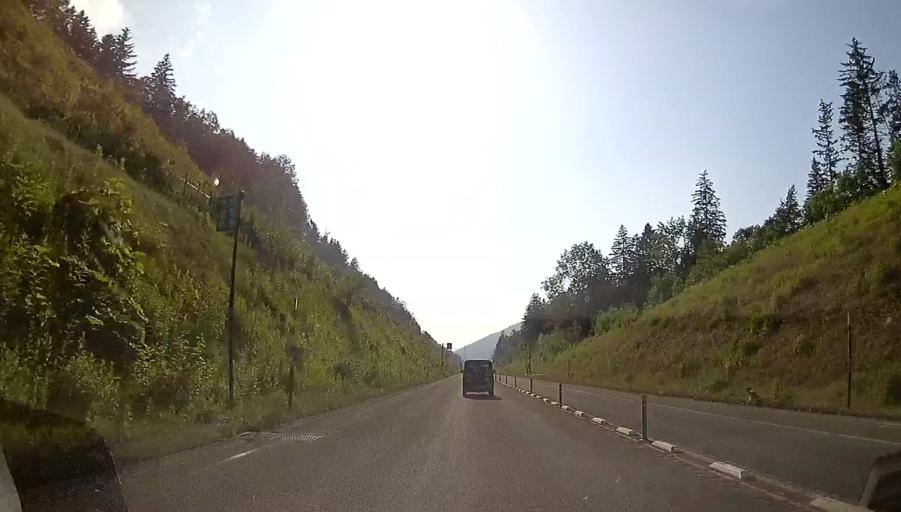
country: JP
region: Hokkaido
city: Shimo-furano
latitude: 43.0523
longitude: 142.6206
